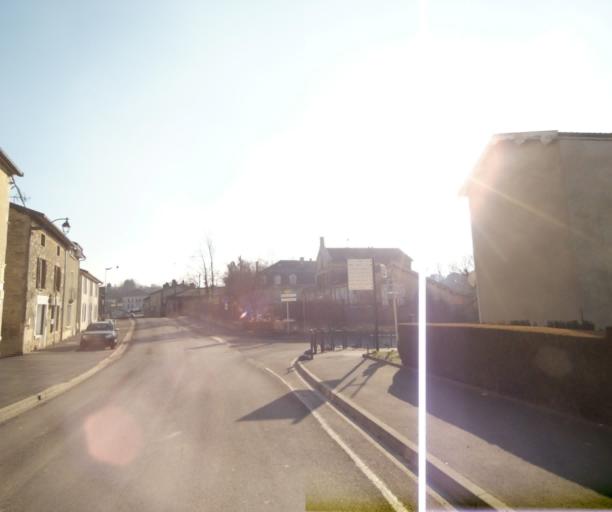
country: FR
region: Champagne-Ardenne
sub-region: Departement de la Haute-Marne
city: Wassy
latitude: 48.4911
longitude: 4.9677
